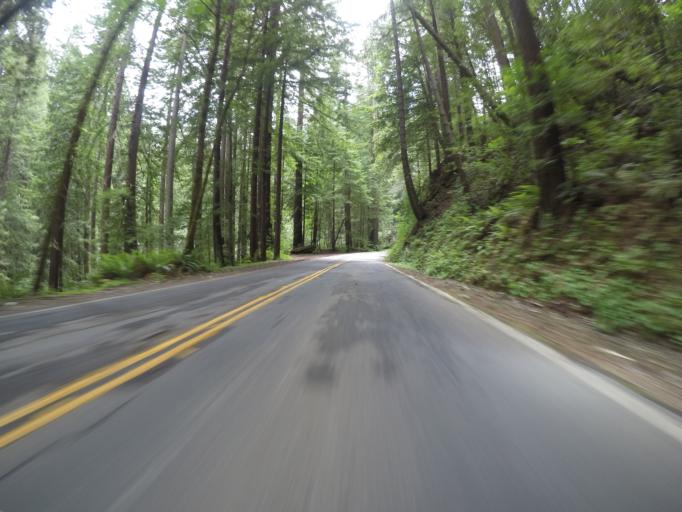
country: US
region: California
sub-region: Humboldt County
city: Rio Dell
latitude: 40.3732
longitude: -123.9248
